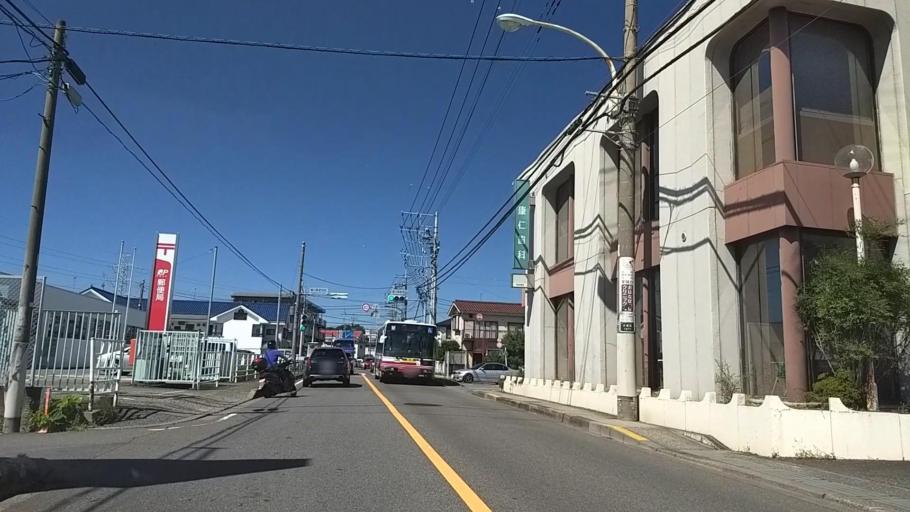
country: JP
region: Tokyo
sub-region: Machida-shi
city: Machida
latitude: 35.5883
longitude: 139.4643
